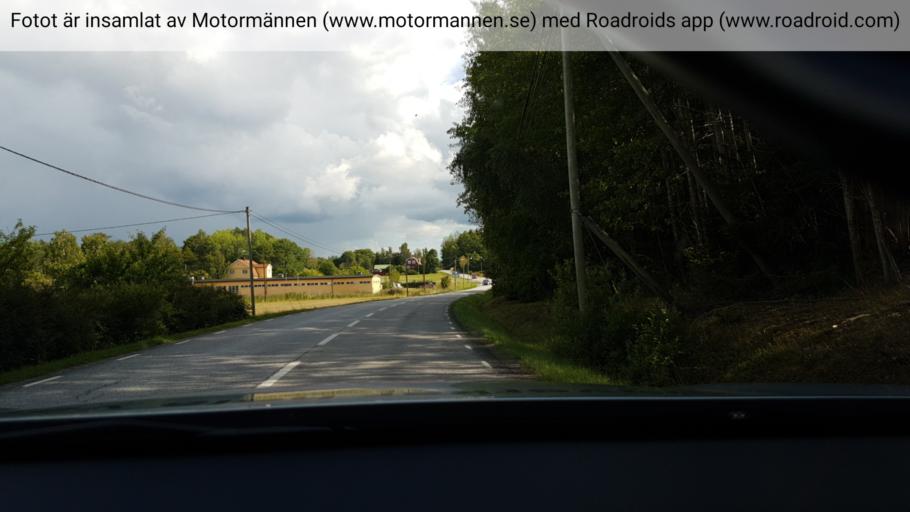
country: SE
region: Stockholm
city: Stenhamra
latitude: 59.3836
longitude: 17.6858
